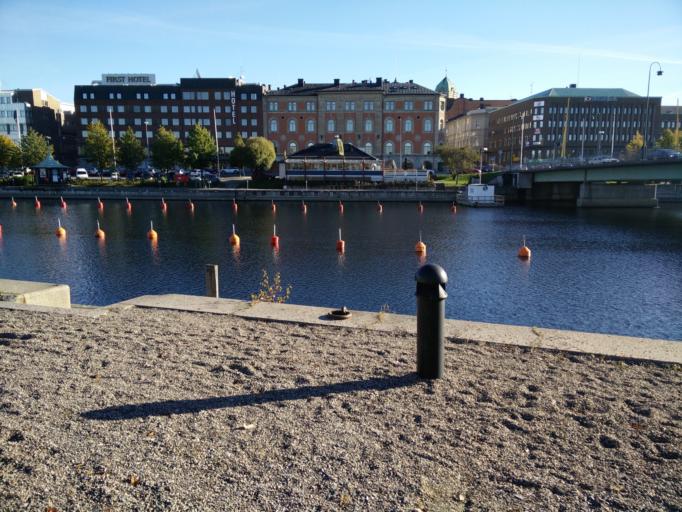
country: SE
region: Vaesternorrland
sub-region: Haernoesands Kommun
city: Haernoesand
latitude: 62.6342
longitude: 17.9360
